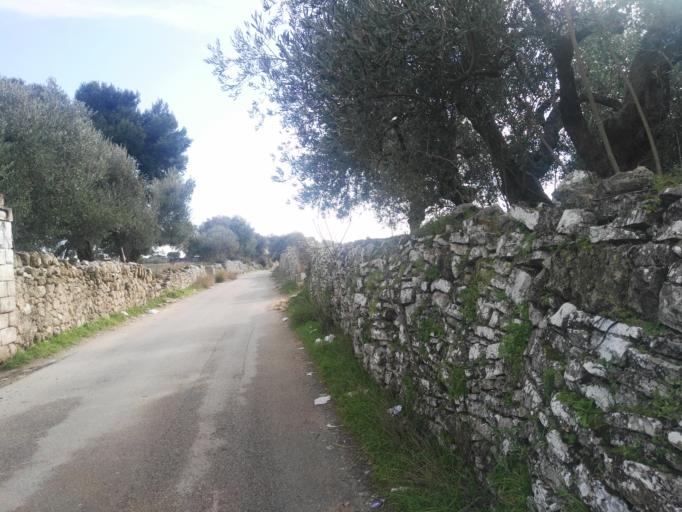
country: IT
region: Apulia
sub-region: Provincia di Barletta - Andria - Trani
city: Andria
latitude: 41.2153
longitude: 16.3071
